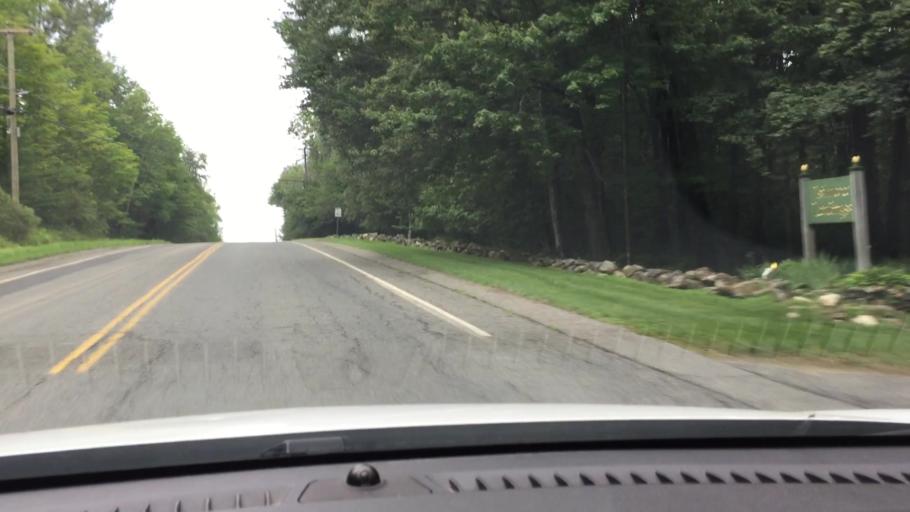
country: US
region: Massachusetts
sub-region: Berkshire County
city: Hinsdale
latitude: 42.4428
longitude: -73.0936
